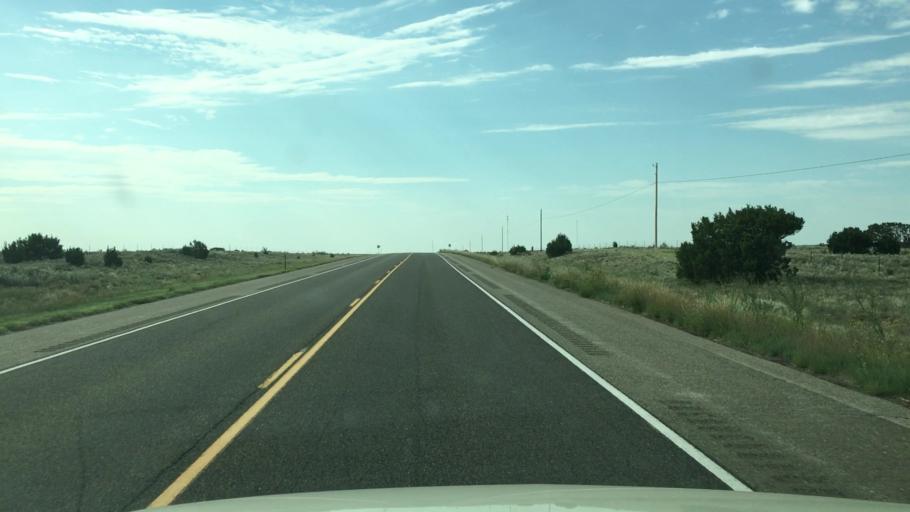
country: US
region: New Mexico
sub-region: Torrance County
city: Moriarty
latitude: 35.0287
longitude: -105.6757
